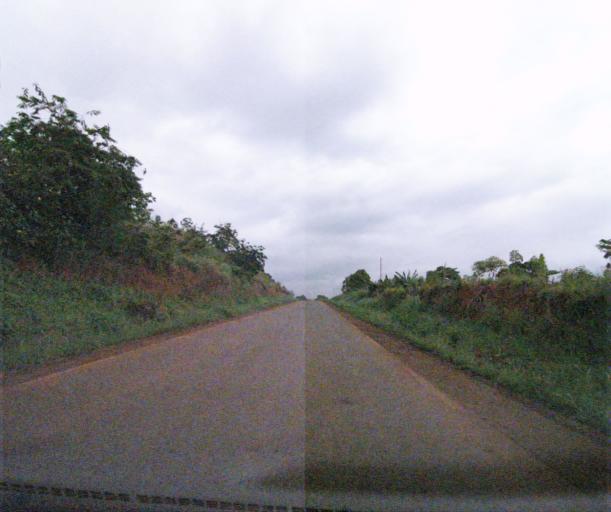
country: CM
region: West
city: Bansoa
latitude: 5.4940
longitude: 10.2238
